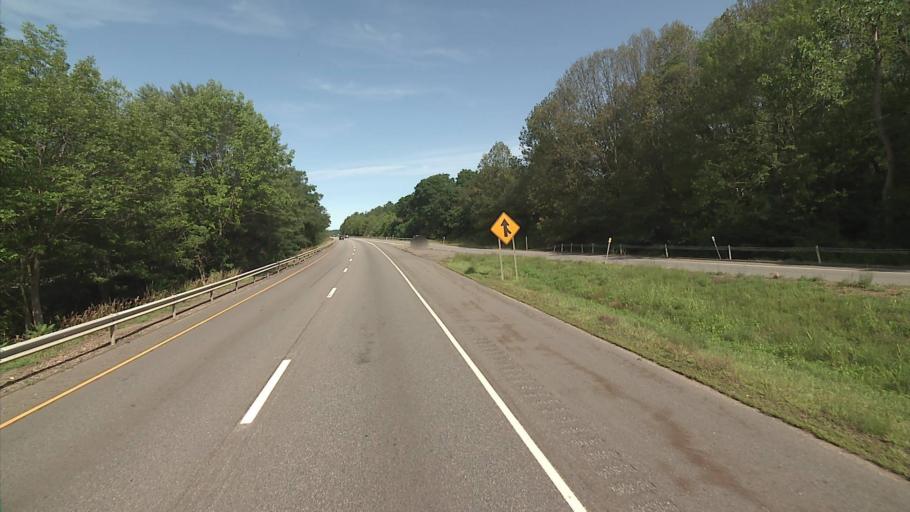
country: US
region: Connecticut
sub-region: New London County
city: Colchester
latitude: 41.5719
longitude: -72.3410
